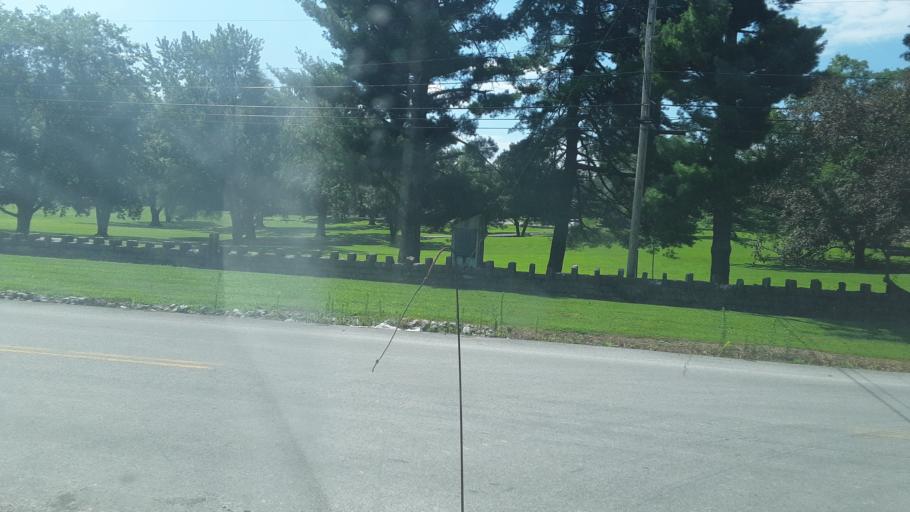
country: US
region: Kentucky
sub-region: Todd County
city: Elkton
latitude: 36.8436
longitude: -87.3006
